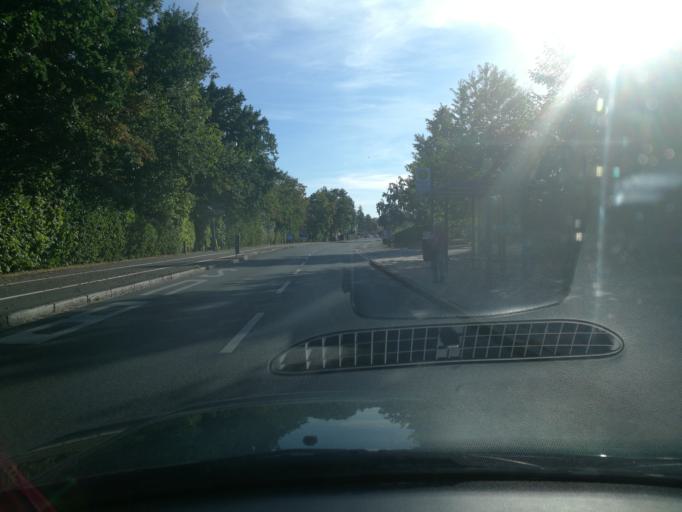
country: DE
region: Bavaria
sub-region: Regierungsbezirk Mittelfranken
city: Erlangen
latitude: 49.5708
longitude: 10.9655
